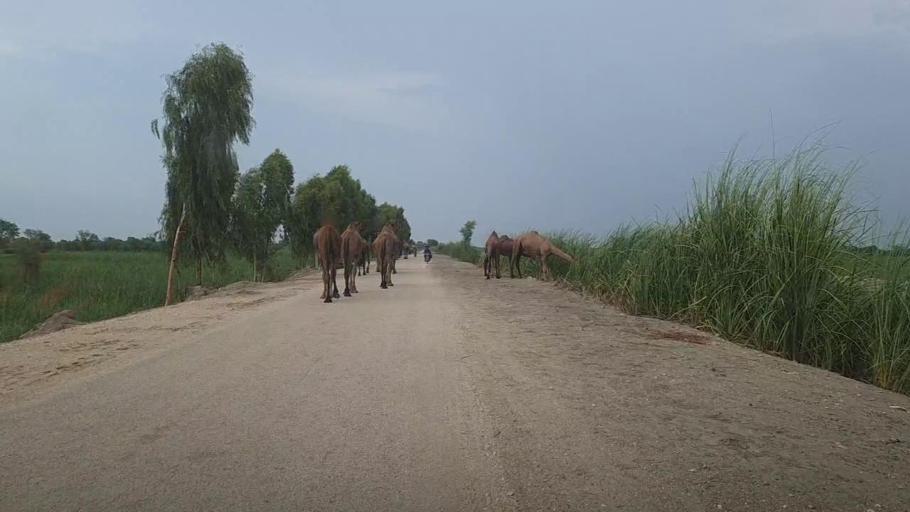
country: PK
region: Sindh
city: Karaundi
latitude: 26.9627
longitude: 68.4262
